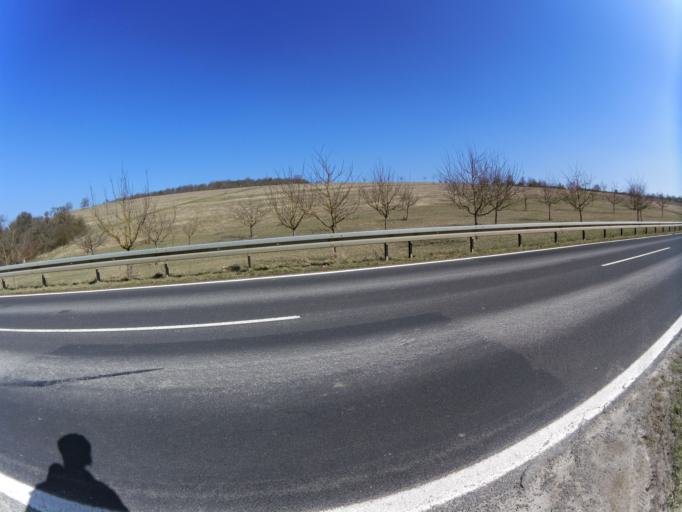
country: DE
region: Bavaria
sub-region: Regierungsbezirk Unterfranken
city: Greussenheim
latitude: 49.8121
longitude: 9.7720
